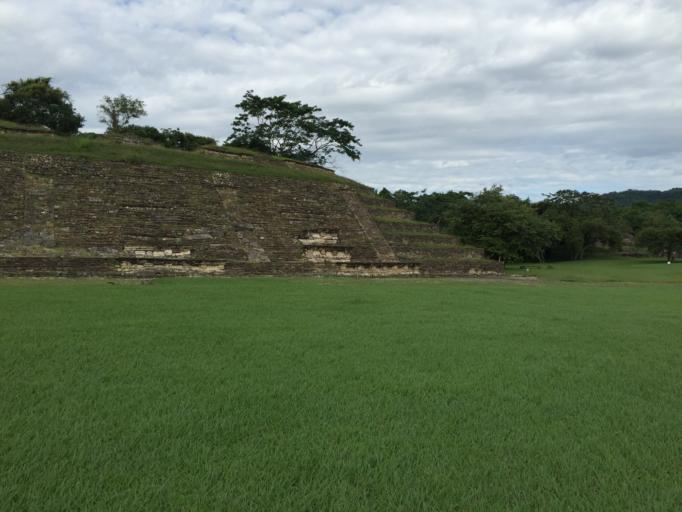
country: MX
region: Veracruz
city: Papantla de Olarte
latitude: 20.4458
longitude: -97.3777
